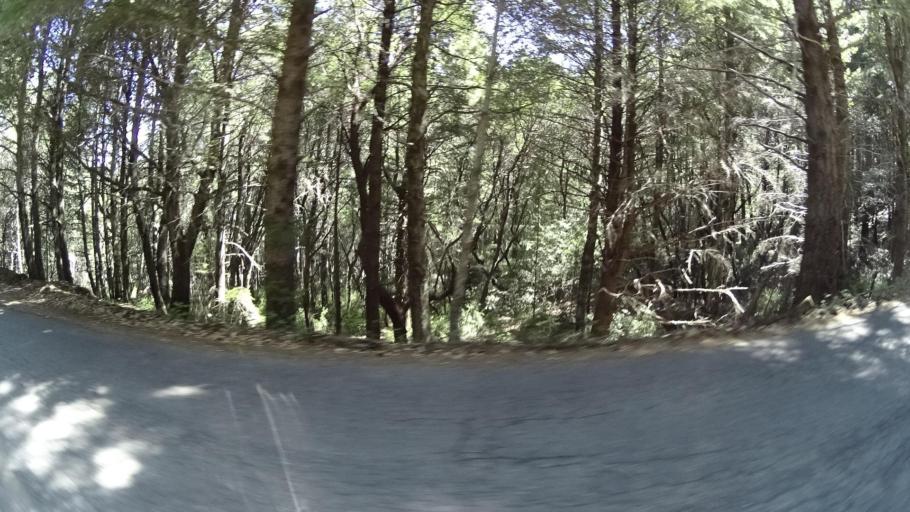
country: US
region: California
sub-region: Humboldt County
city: Redway
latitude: 40.1294
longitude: -123.9765
